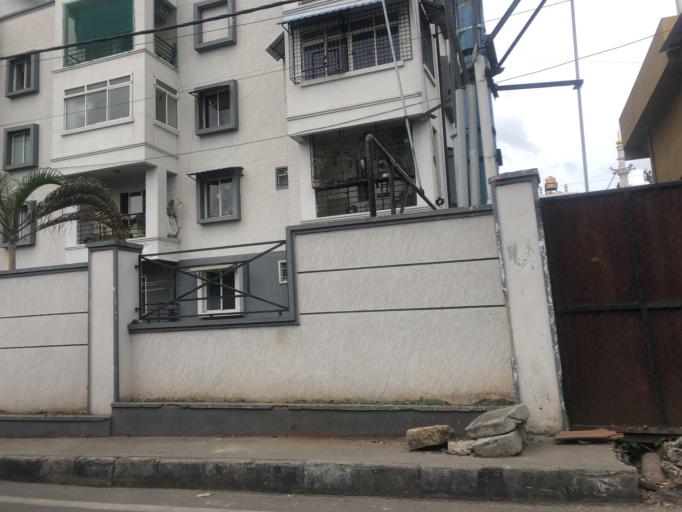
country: IN
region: Karnataka
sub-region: Bangalore Urban
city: Bangalore
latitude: 12.9481
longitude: 77.5388
